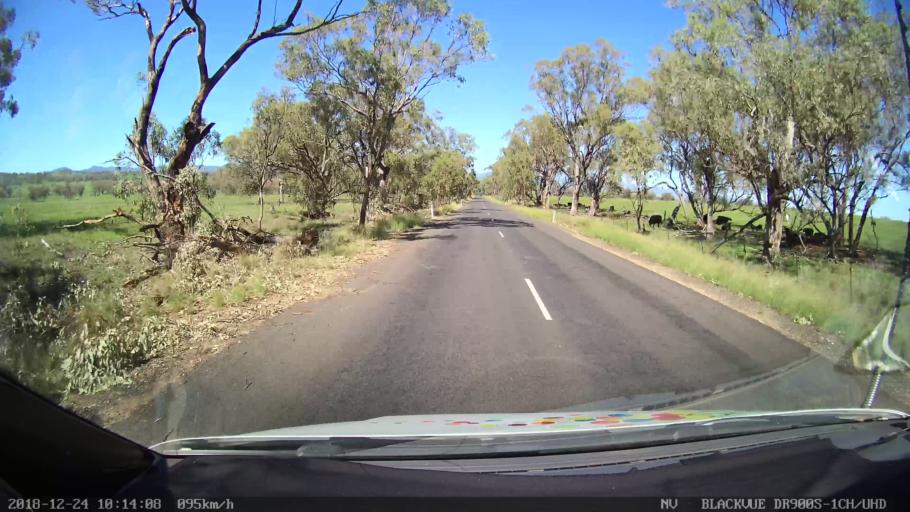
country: AU
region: New South Wales
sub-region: Liverpool Plains
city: Quirindi
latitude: -31.6954
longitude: 150.6322
